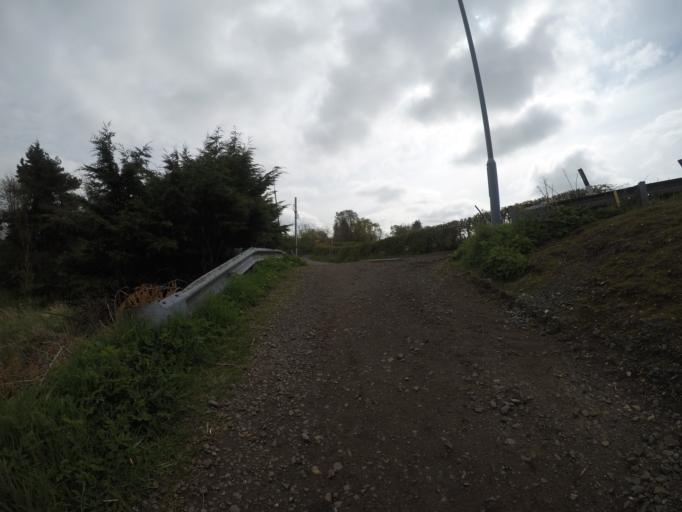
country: GB
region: Scotland
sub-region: East Renfrewshire
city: Newton Mearns
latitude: 55.7614
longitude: -4.3136
